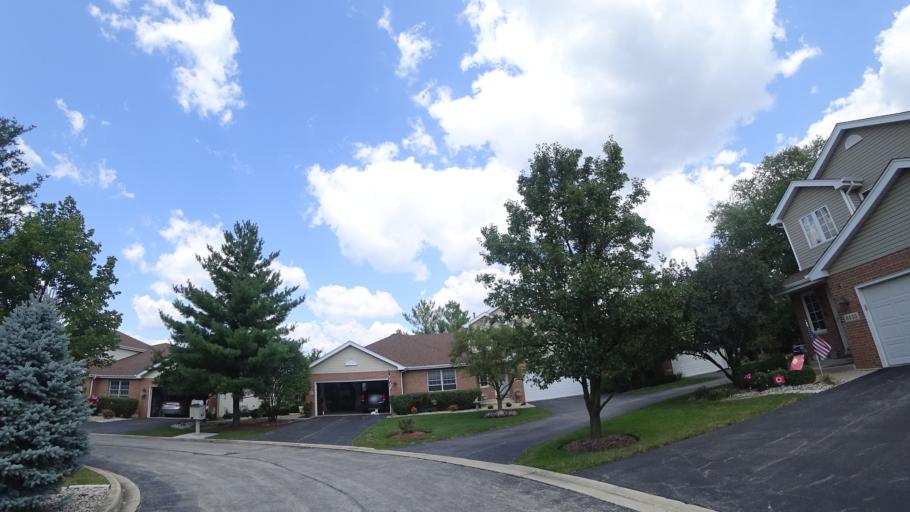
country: US
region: Illinois
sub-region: Cook County
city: Palos Heights
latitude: 41.6257
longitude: -87.7840
